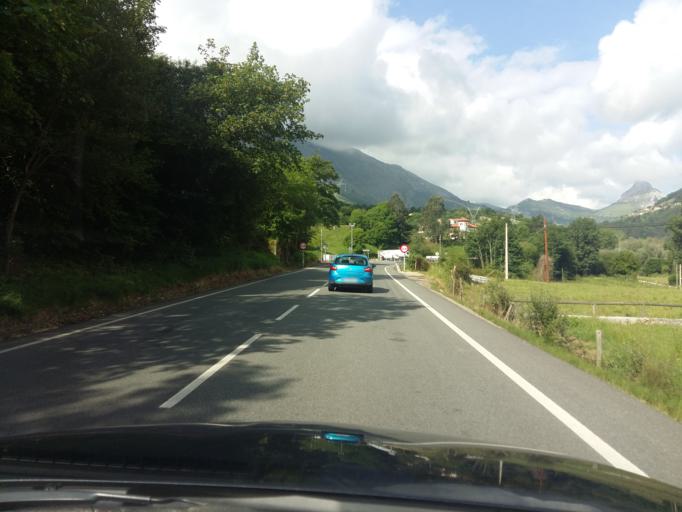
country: ES
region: Cantabria
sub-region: Provincia de Cantabria
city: Tresviso
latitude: 43.3204
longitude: -4.5915
